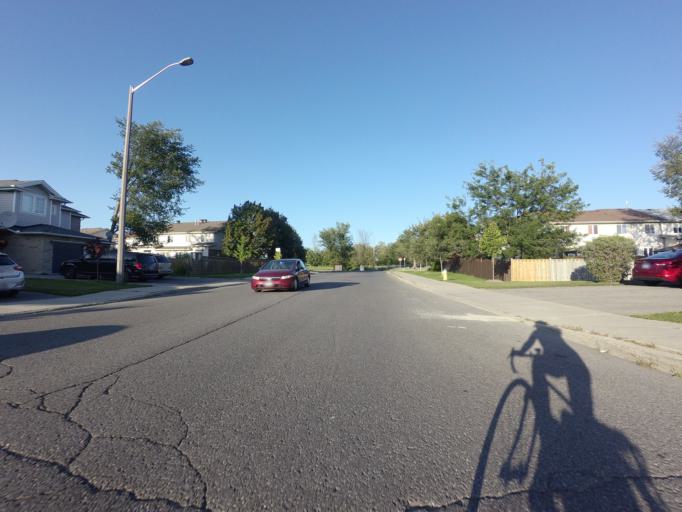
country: CA
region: Ontario
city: Bells Corners
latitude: 45.2817
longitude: -75.7312
